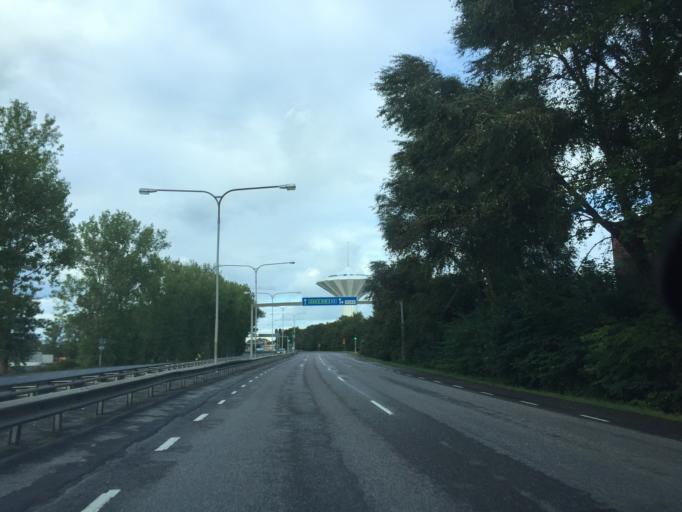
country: SE
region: OErebro
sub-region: Orebro Kommun
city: Orebro
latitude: 59.2860
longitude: 15.2194
